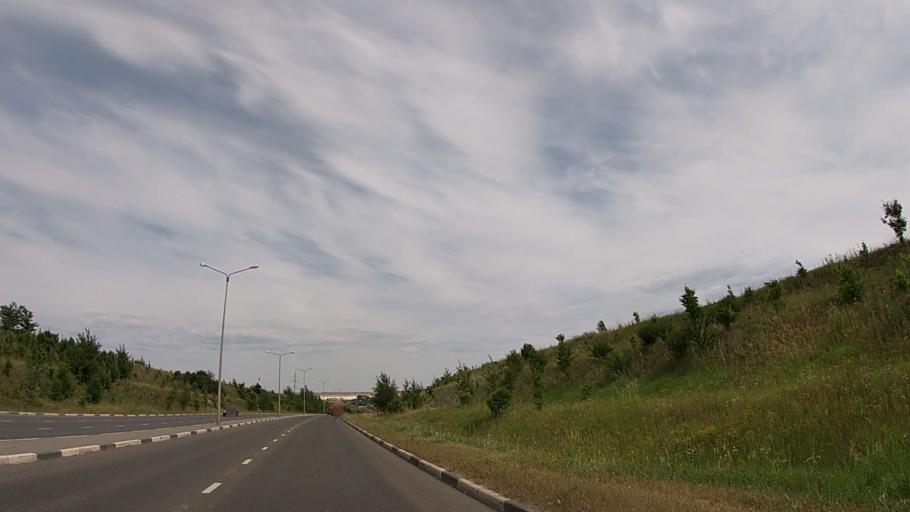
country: RU
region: Belgorod
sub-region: Belgorodskiy Rayon
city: Belgorod
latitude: 50.6023
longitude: 36.5299
